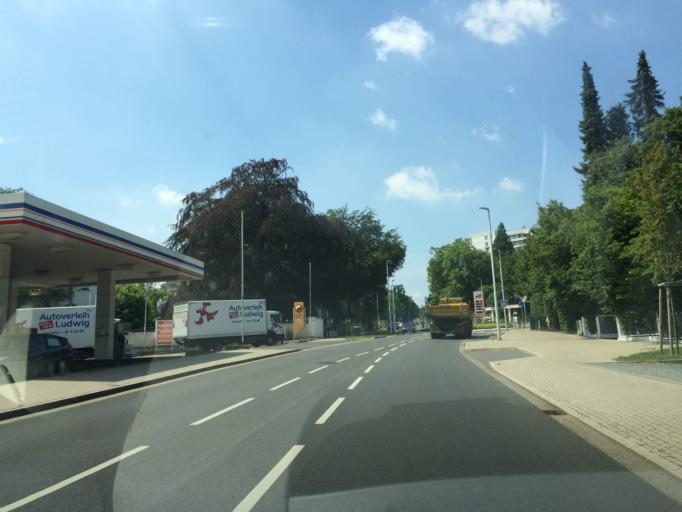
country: DE
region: North Rhine-Westphalia
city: Iserlohn
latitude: 51.3724
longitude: 7.7182
